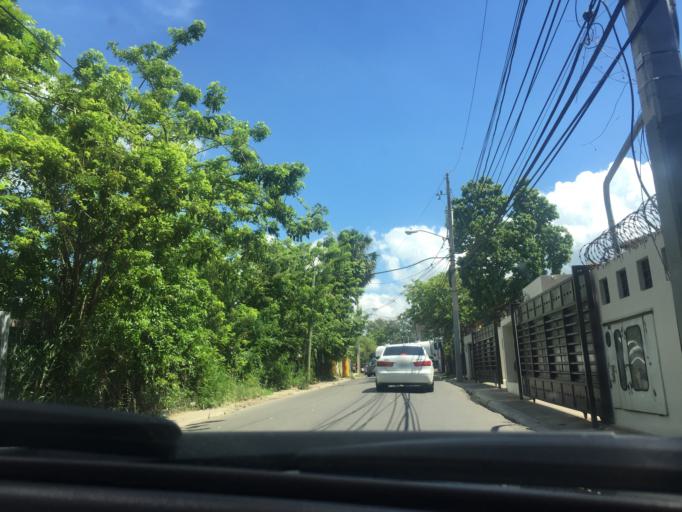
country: DO
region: Santiago
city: Santiago de los Caballeros
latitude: 19.4607
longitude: -70.6600
